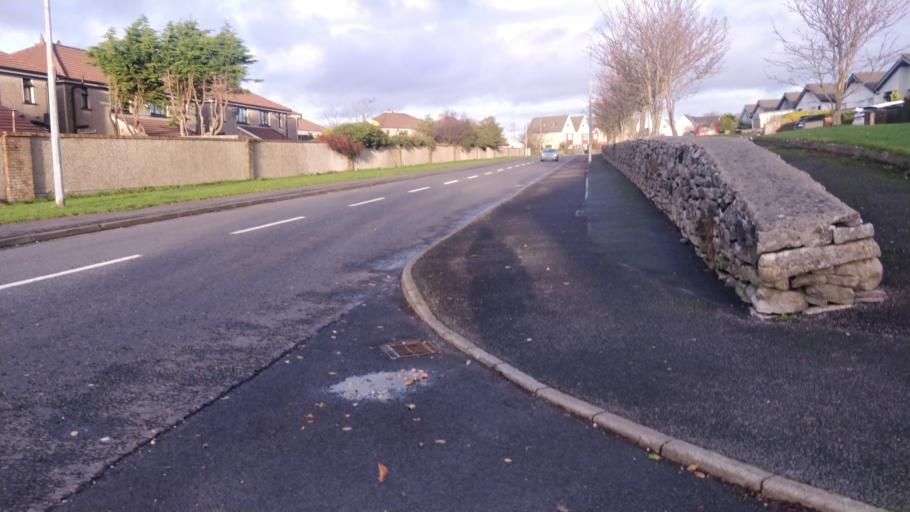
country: IE
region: Connaught
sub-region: County Galway
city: Gaillimh
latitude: 53.2900
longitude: -8.9975
